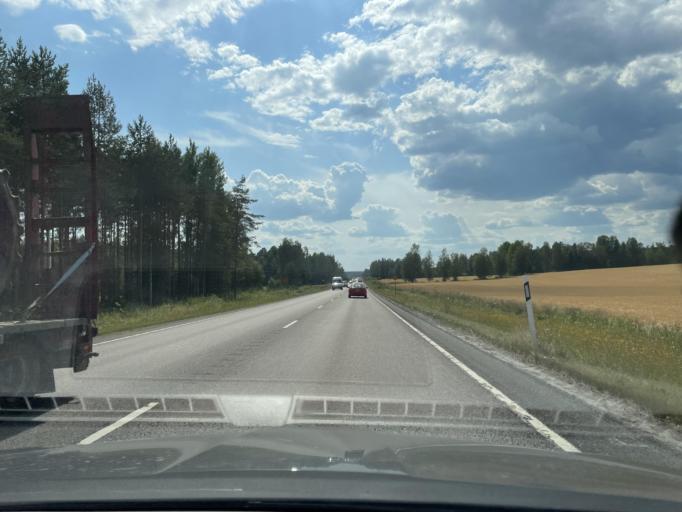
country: FI
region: Central Finland
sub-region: Jyvaeskylae
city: Korpilahti
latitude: 61.9758
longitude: 25.3977
